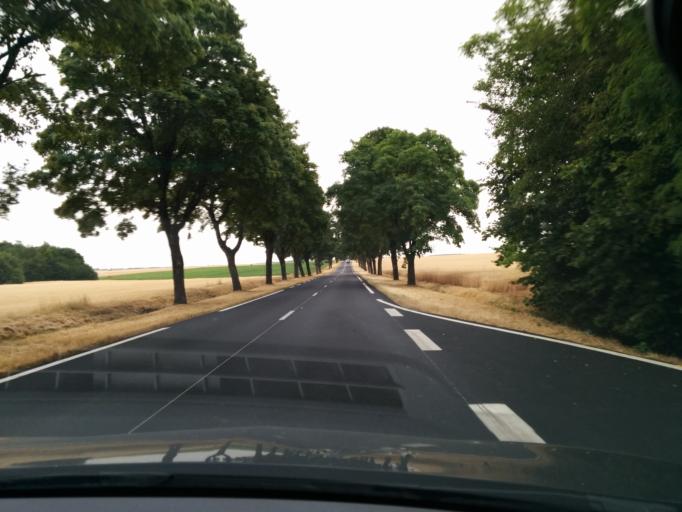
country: FR
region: Ile-de-France
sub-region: Departement de l'Essonne
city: Pussay
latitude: 48.4015
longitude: 1.9704
